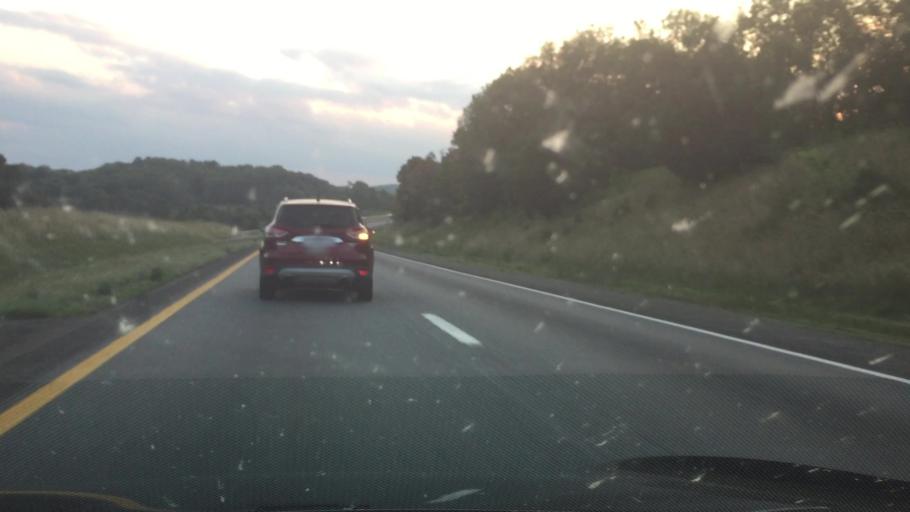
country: US
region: Virginia
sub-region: City of Radford
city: Radford
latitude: 37.0989
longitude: -80.5306
